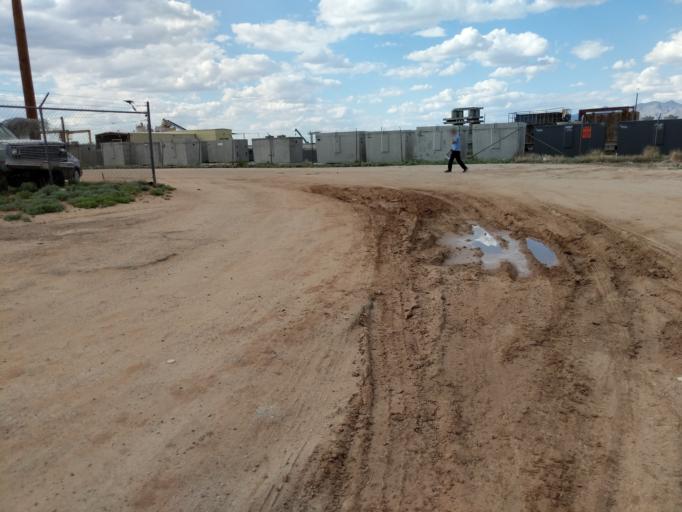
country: US
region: Arizona
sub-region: Pima County
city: Tucson
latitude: 32.1593
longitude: -110.8879
